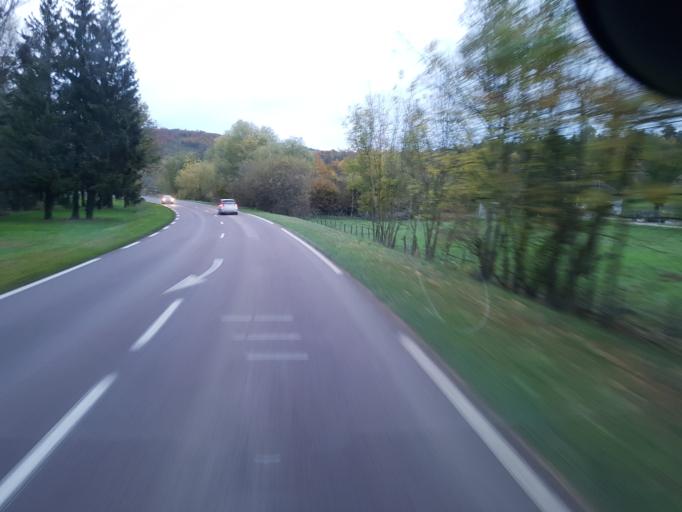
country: FR
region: Champagne-Ardenne
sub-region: Departement de l'Aube
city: Mussy-sur-Seine
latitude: 47.9767
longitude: 4.5012
